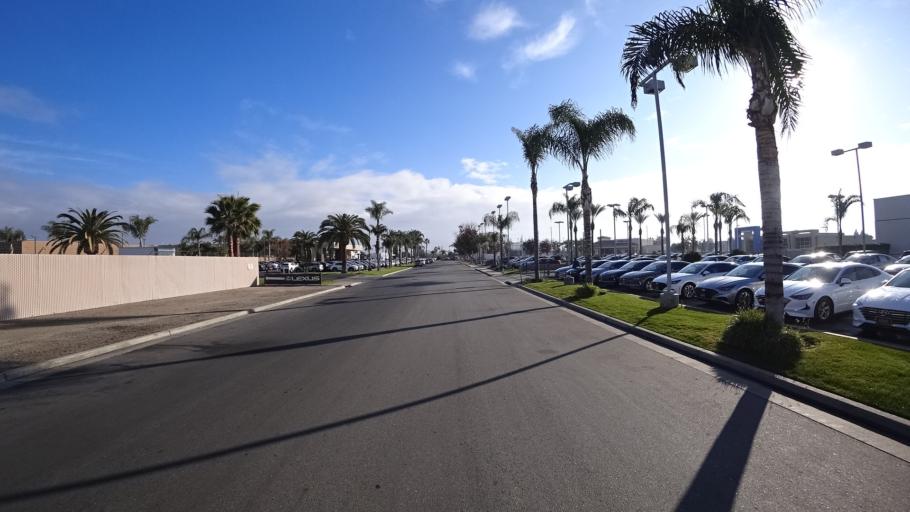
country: US
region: California
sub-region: Kern County
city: Greenfield
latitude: 35.3072
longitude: -119.0377
